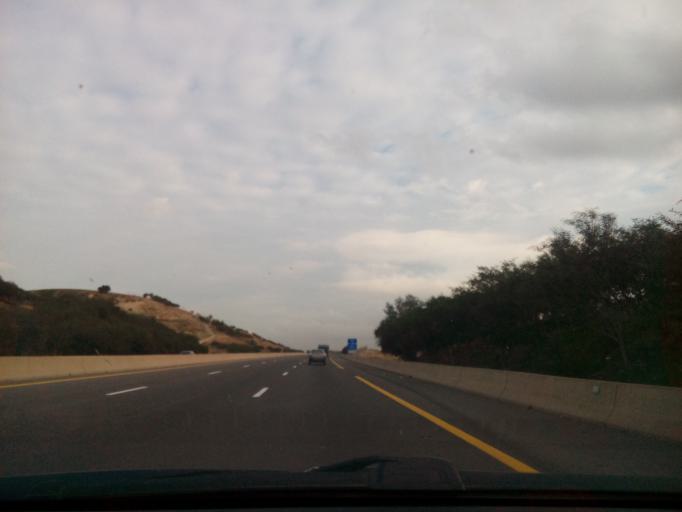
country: DZ
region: Mostaganem
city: Mostaganem
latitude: 35.7050
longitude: 0.2314
